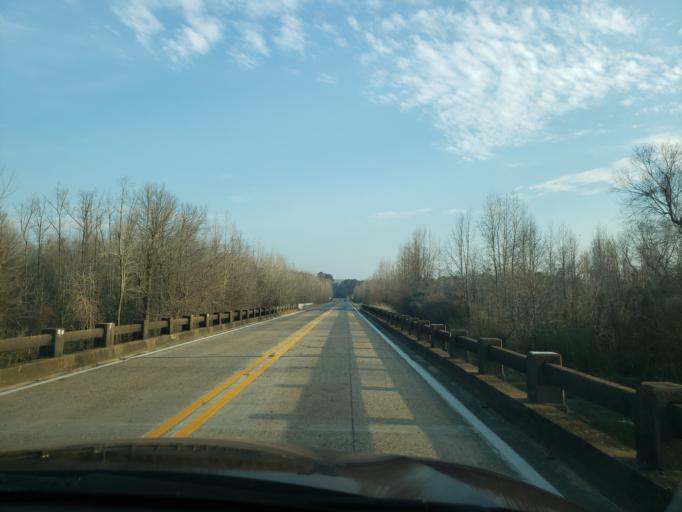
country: US
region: Alabama
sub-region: Hale County
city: Greensboro
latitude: 32.8298
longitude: -87.6043
